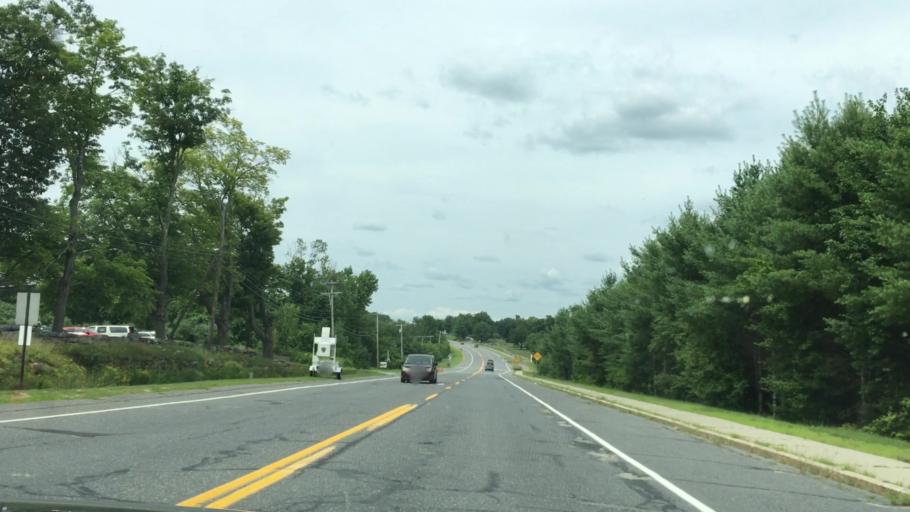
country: US
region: Massachusetts
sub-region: Worcester County
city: Gardner
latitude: 42.5889
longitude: -71.9867
